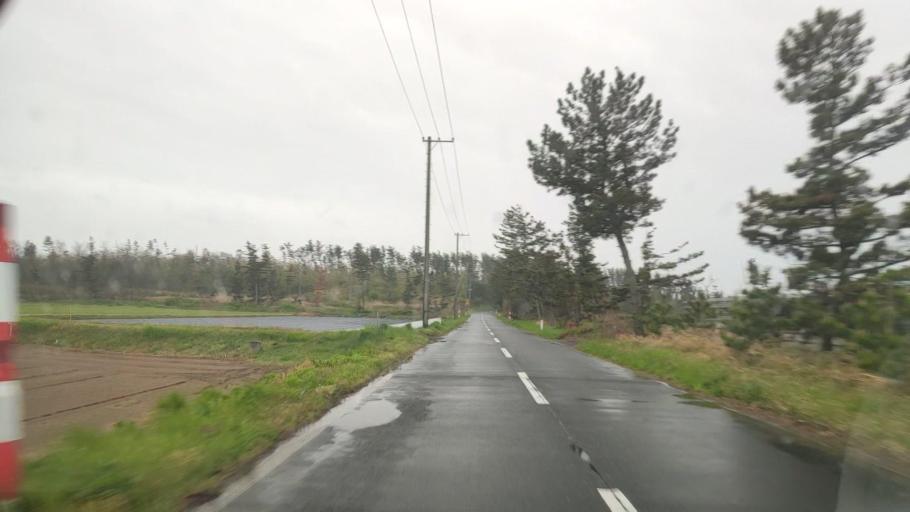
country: JP
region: Akita
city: Noshiromachi
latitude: 40.0966
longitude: 139.9660
